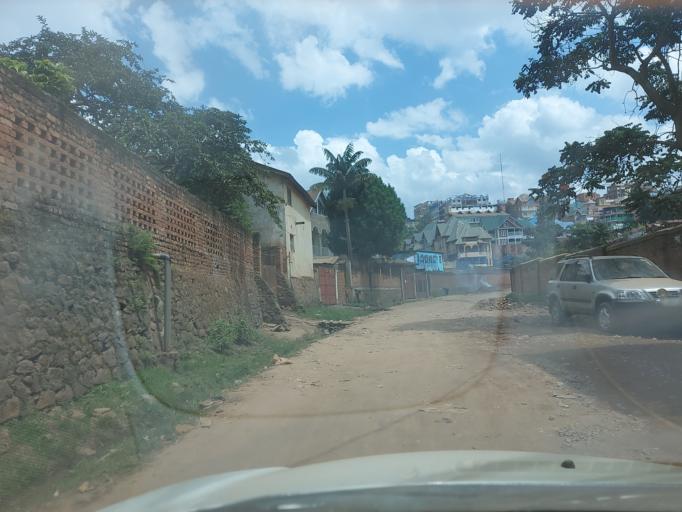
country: CD
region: South Kivu
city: Bukavu
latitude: -2.5054
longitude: 28.8621
